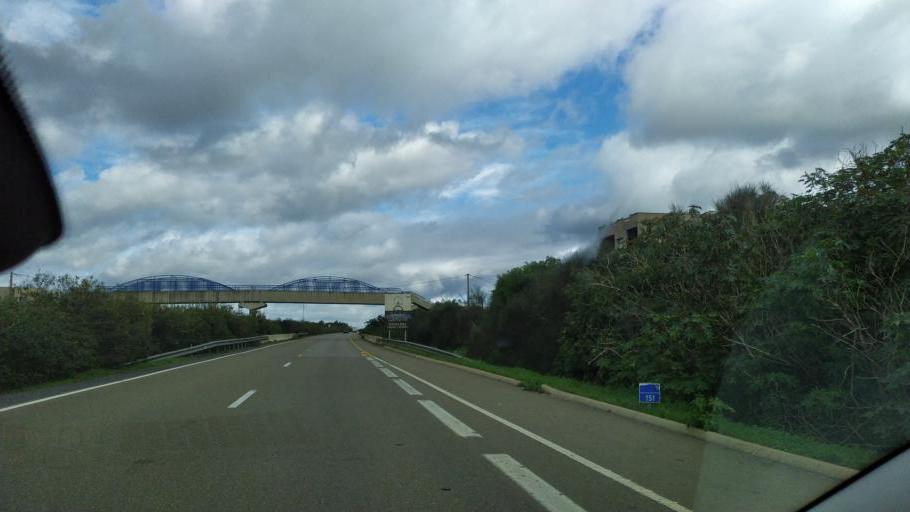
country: MA
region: Gharb-Chrarda-Beni Hssen
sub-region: Kenitra Province
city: Lalla Mimouna
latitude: 34.8630
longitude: -6.2206
